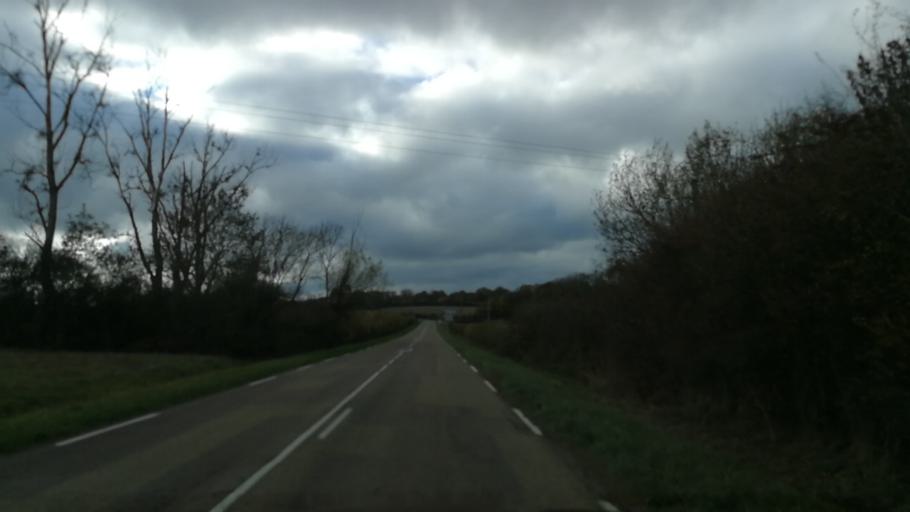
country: FR
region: Bourgogne
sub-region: Departement de la Cote-d'Or
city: Saulieu
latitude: 47.2689
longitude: 4.3571
